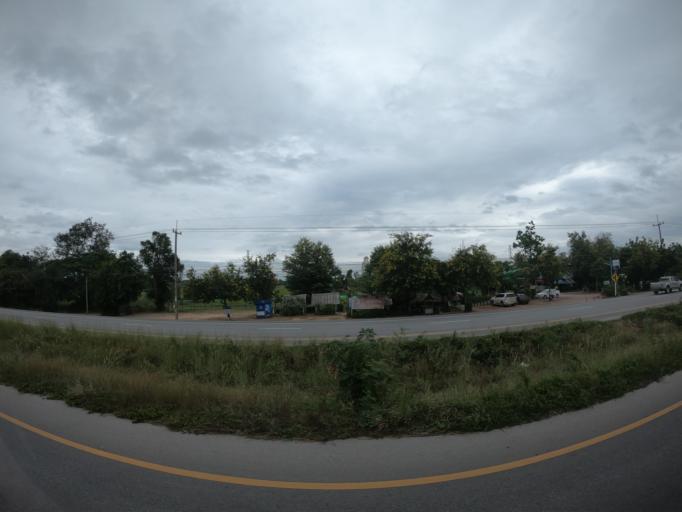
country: TH
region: Roi Et
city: Changhan
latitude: 16.1063
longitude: 103.5150
